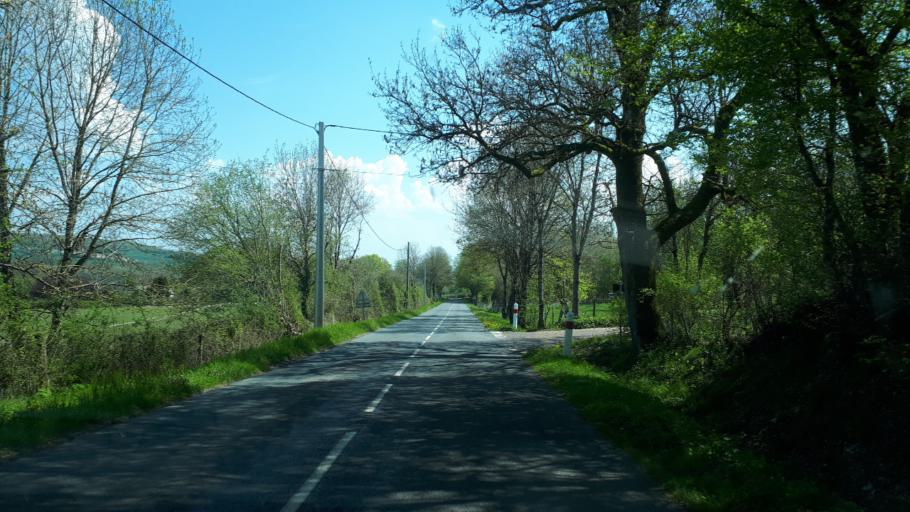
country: FR
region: Centre
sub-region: Departement du Cher
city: Henrichemont
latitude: 47.3046
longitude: 2.6237
